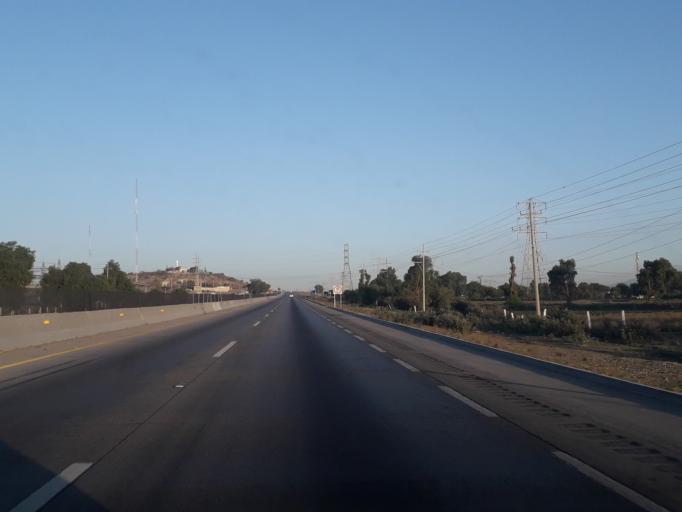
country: MX
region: Puebla
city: Acatzingo de Hidalgo
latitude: 18.9702
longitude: -97.7907
